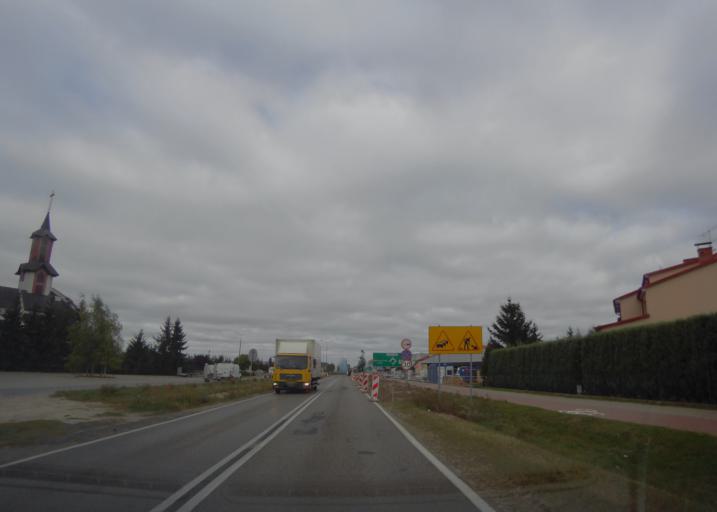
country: PL
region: Lublin Voivodeship
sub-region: Powiat wlodawski
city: Wlodawa
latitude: 51.5451
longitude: 23.5421
